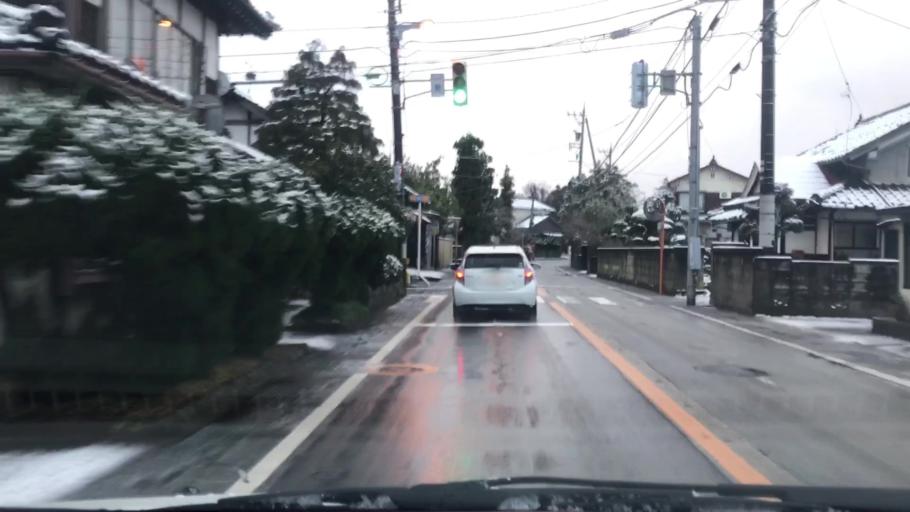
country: JP
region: Toyama
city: Kamiichi
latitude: 36.7006
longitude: 137.3262
